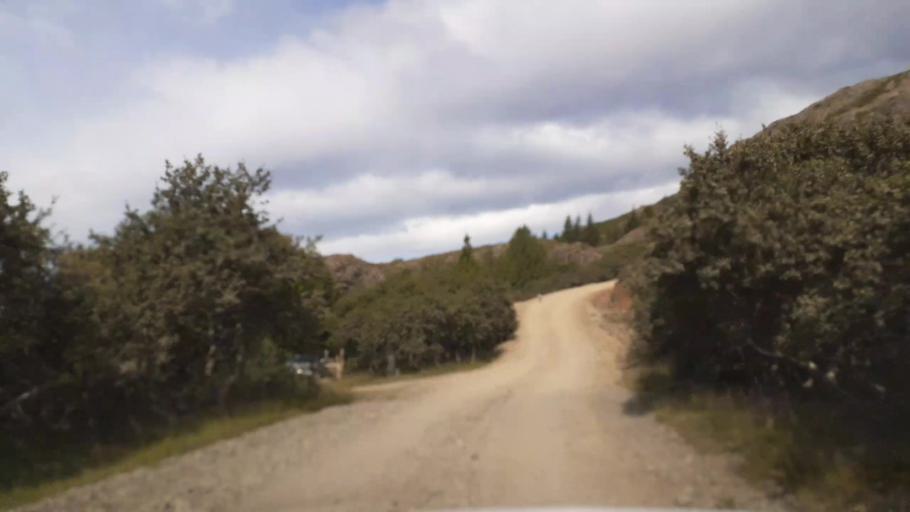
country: IS
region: East
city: Hoefn
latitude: 64.4377
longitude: -14.9114
